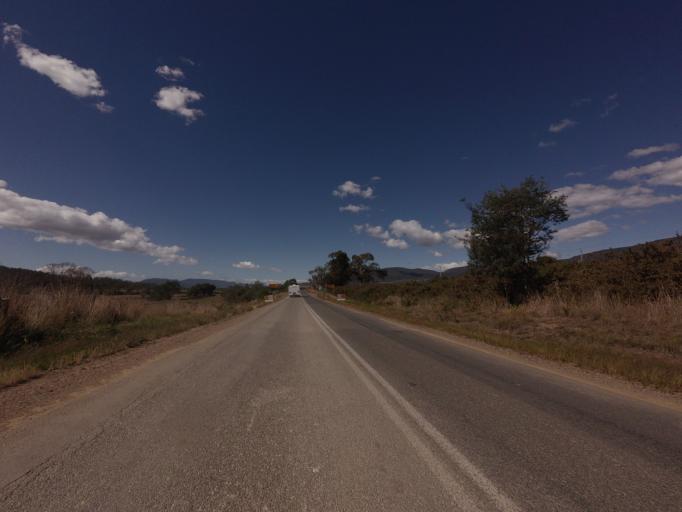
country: AU
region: Tasmania
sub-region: Break O'Day
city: St Helens
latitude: -41.6473
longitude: 147.9369
